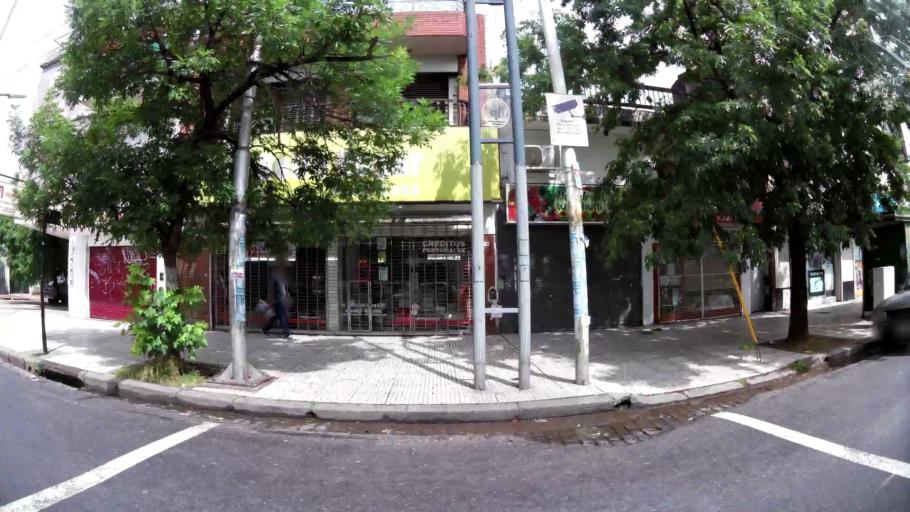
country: AR
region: Buenos Aires
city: Caseros
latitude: -34.6178
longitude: -58.5298
